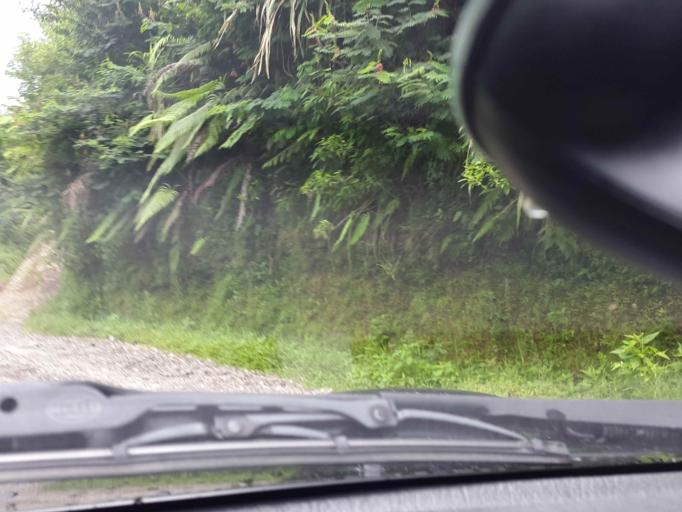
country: ID
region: Central Java
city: Wonosobo
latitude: -7.3562
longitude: 110.0203
